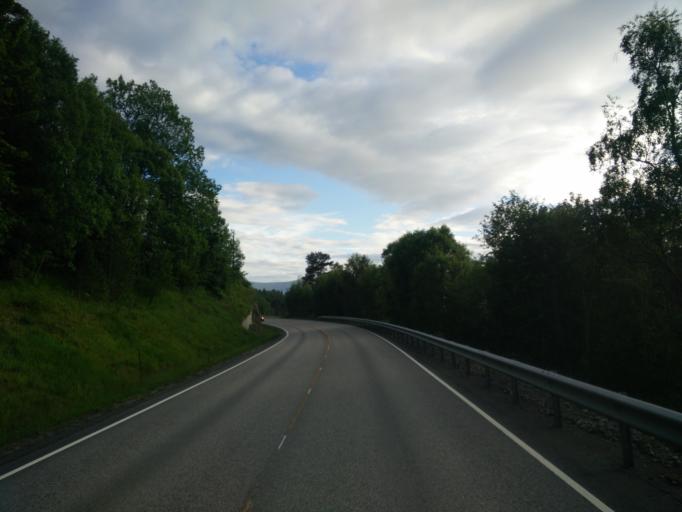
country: NO
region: More og Romsdal
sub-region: Kristiansund
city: Rensvik
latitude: 63.0168
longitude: 8.0048
